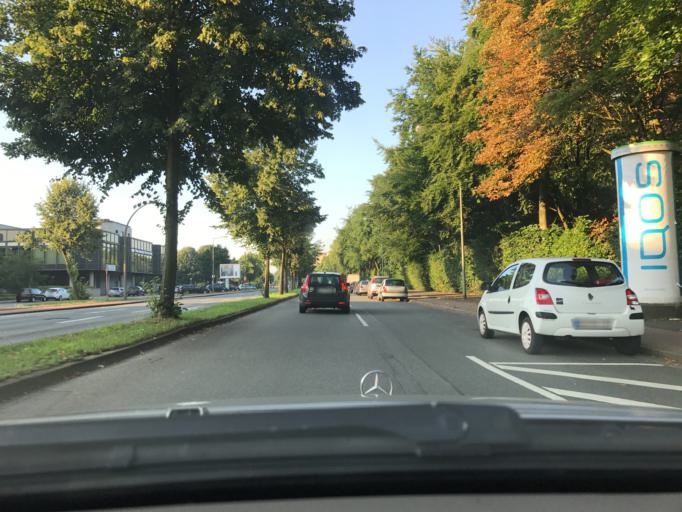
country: DE
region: North Rhine-Westphalia
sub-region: Regierungsbezirk Dusseldorf
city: Hochfeld
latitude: 51.4030
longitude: 6.7107
